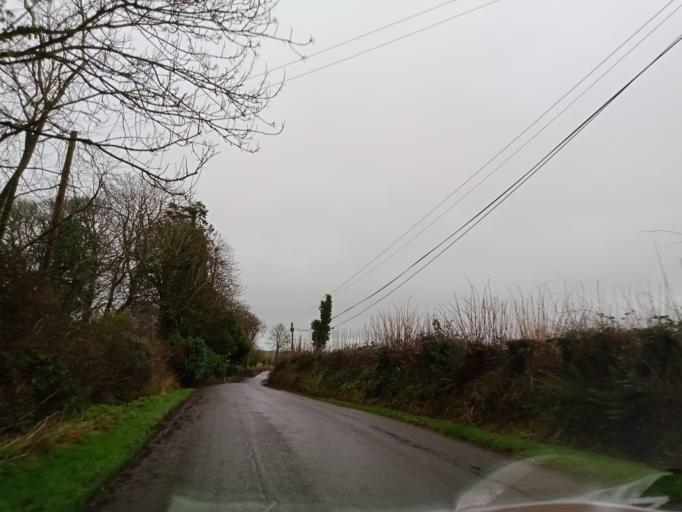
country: IE
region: Munster
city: Fethard
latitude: 52.5576
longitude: -7.6971
